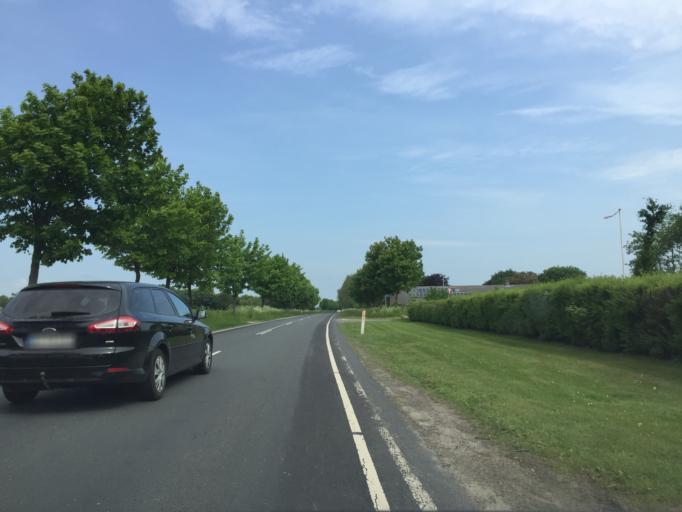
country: DK
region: South Denmark
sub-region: Nyborg Kommune
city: Nyborg
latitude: 55.2046
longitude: 10.7274
